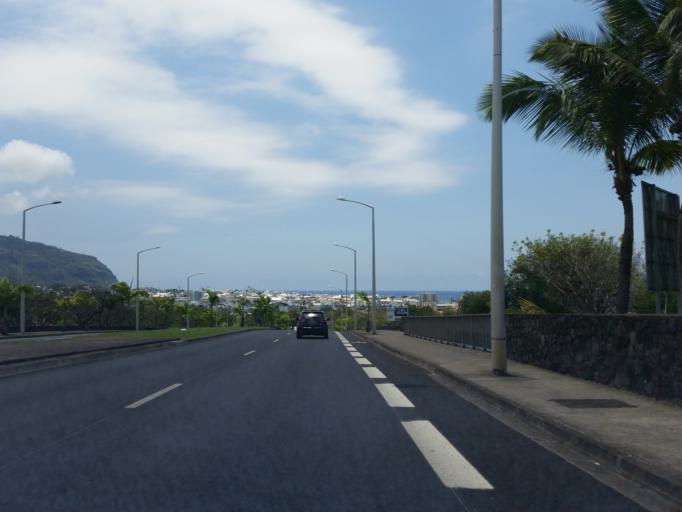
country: RE
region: Reunion
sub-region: Reunion
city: Saint-Denis
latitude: -20.8956
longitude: 55.4732
